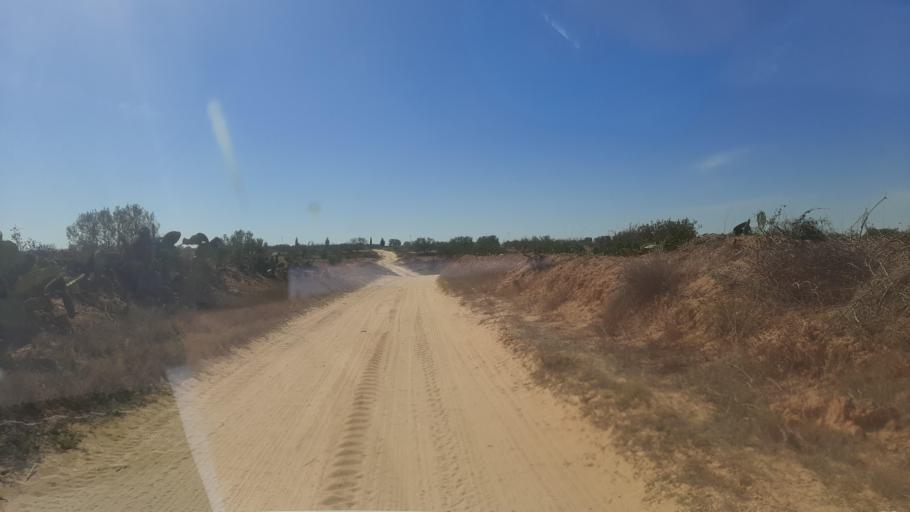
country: TN
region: Safaqis
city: Sfax
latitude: 34.8341
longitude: 10.5574
